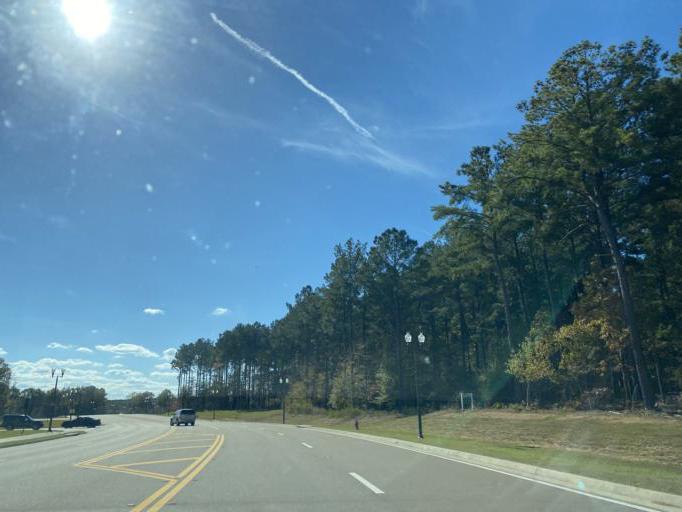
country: US
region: Mississippi
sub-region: Madison County
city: Madison
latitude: 32.4657
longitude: -90.1268
